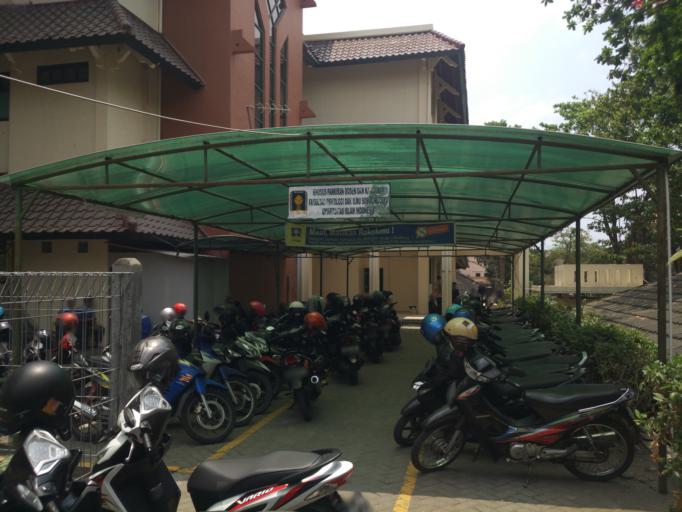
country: ID
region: Daerah Istimewa Yogyakarta
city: Sleman
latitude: -7.6875
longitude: 110.4140
